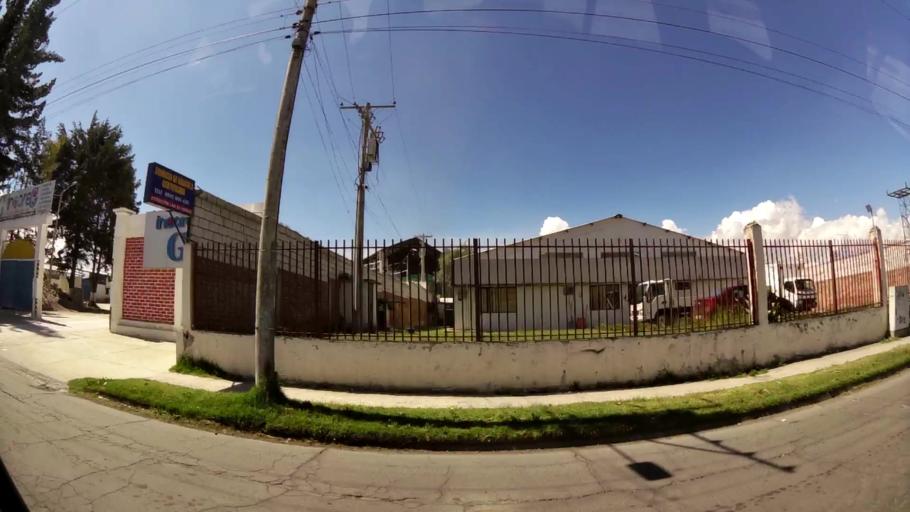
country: EC
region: Chimborazo
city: Riobamba
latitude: -1.6805
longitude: -78.6319
